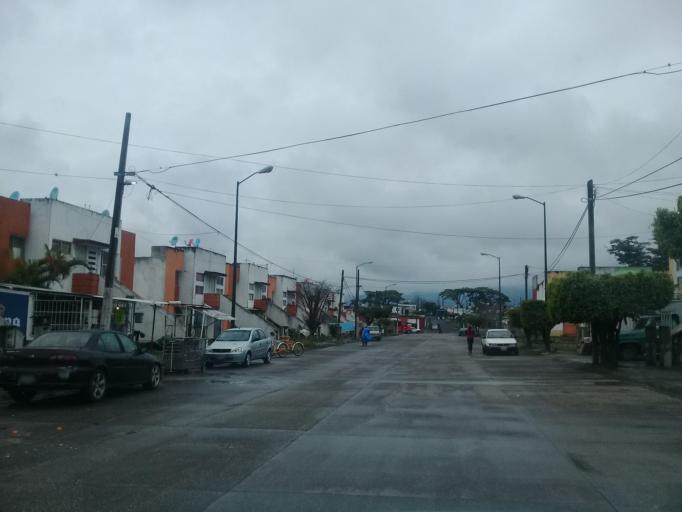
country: MX
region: Veracruz
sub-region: Cordoba
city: San Jose de Tapia
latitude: 18.8386
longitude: -96.9533
